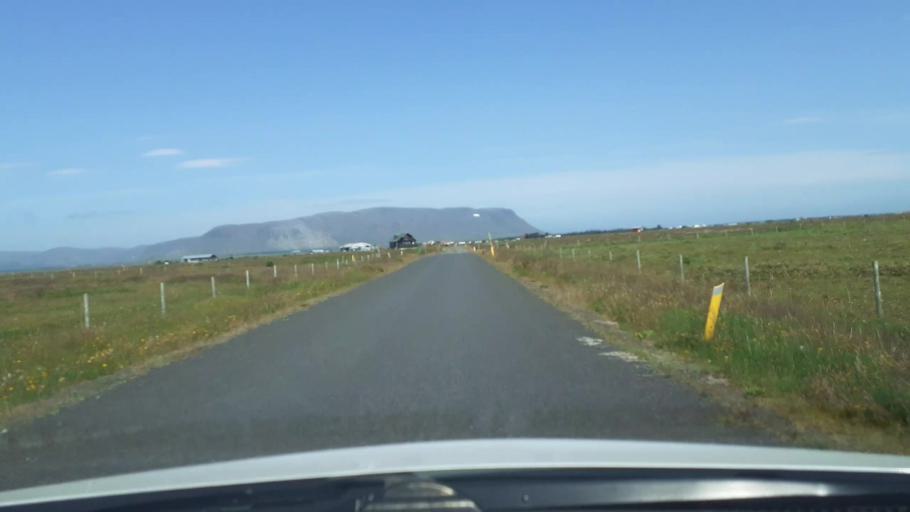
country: IS
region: South
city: Selfoss
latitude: 63.8953
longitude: -21.0813
